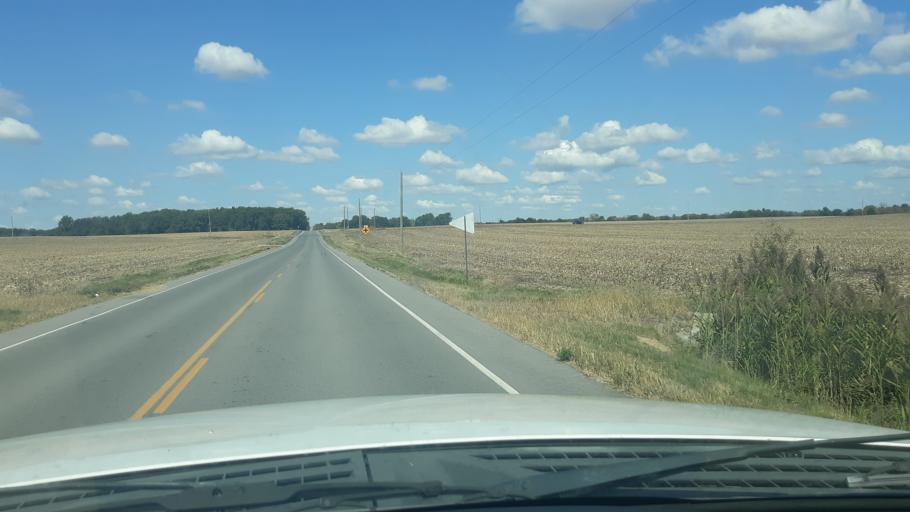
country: US
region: Illinois
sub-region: Saline County
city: Eldorado
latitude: 37.8017
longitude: -88.4848
